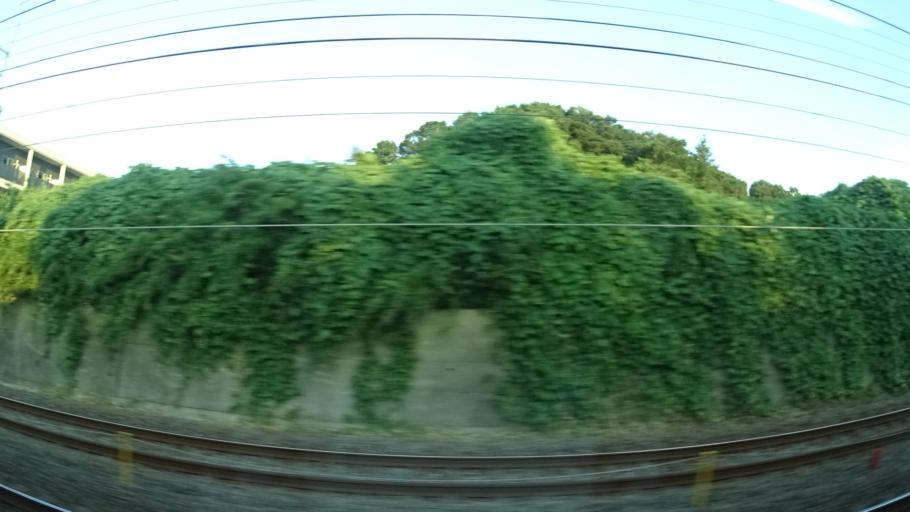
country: JP
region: Chiba
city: Abiko
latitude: 35.8742
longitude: 140.0487
